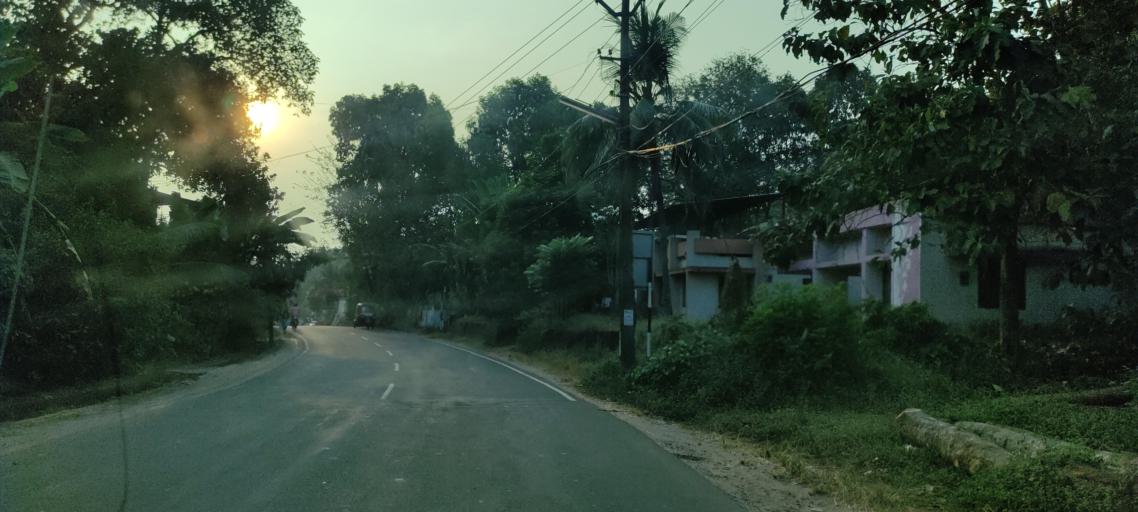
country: IN
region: Kerala
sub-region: Alappuzha
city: Mavelikara
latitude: 9.2554
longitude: 76.5655
